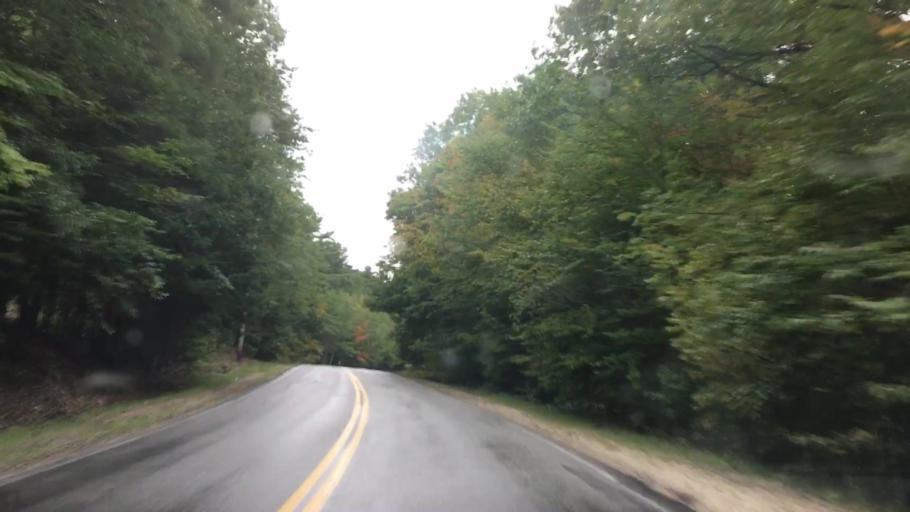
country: US
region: Maine
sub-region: Cumberland County
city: Raymond
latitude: 43.9307
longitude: -70.4073
